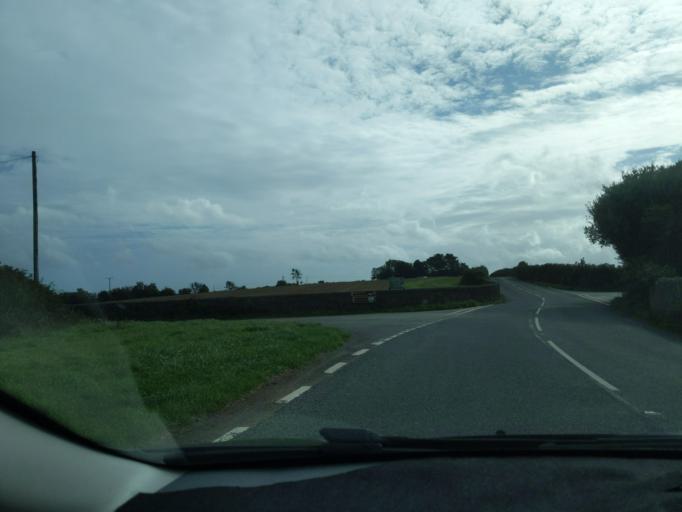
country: GB
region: England
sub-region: Cornwall
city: Mevagissey
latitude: 50.2689
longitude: -4.8306
